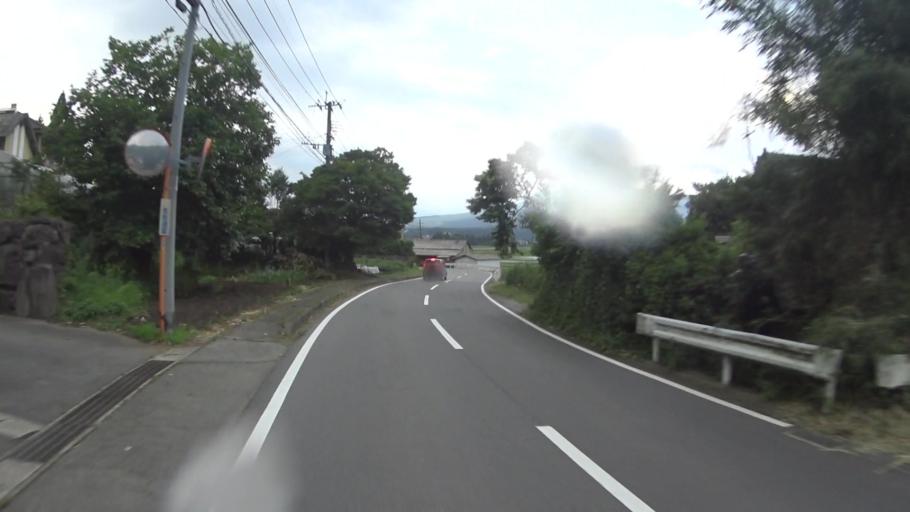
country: JP
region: Kumamoto
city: Aso
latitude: 32.9164
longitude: 130.9767
